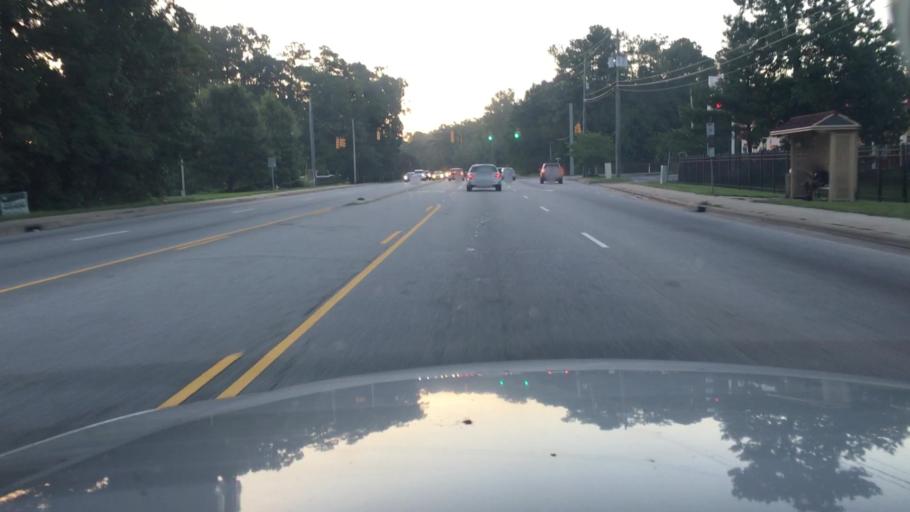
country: US
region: North Carolina
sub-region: Cumberland County
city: Fort Bragg
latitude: 35.0584
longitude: -79.0038
